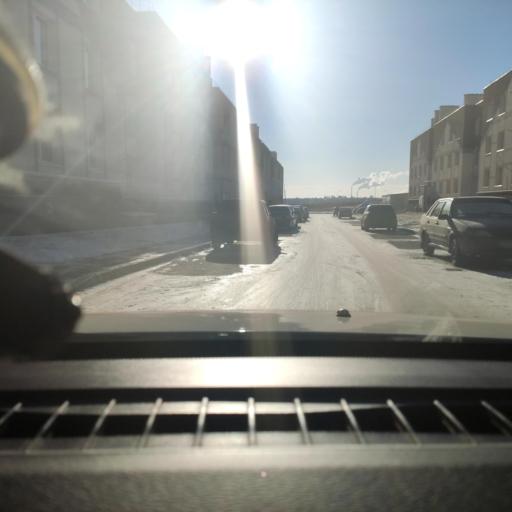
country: RU
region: Samara
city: Petra-Dubrava
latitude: 53.3062
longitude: 50.3143
